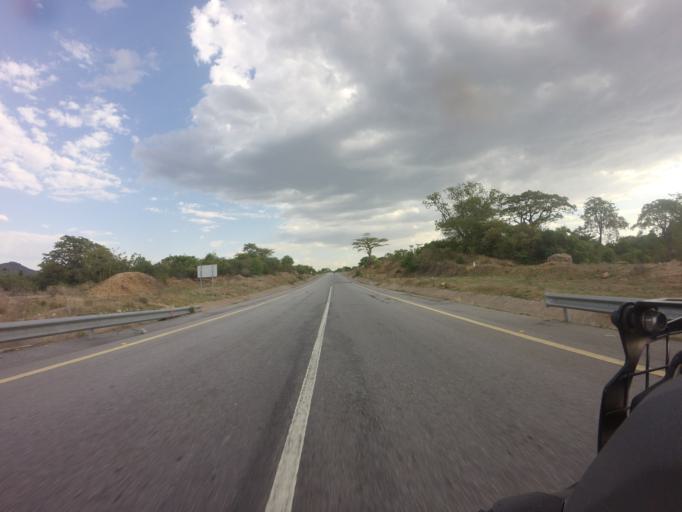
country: AO
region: Huila
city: Lubango
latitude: -14.3673
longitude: 14.0396
